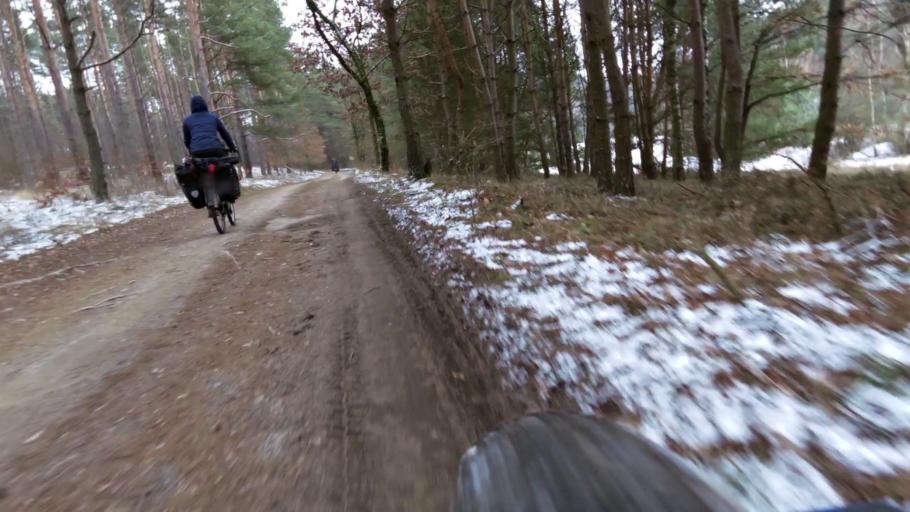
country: PL
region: West Pomeranian Voivodeship
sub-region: Powiat walecki
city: Miroslawiec
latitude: 53.3222
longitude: 16.0875
